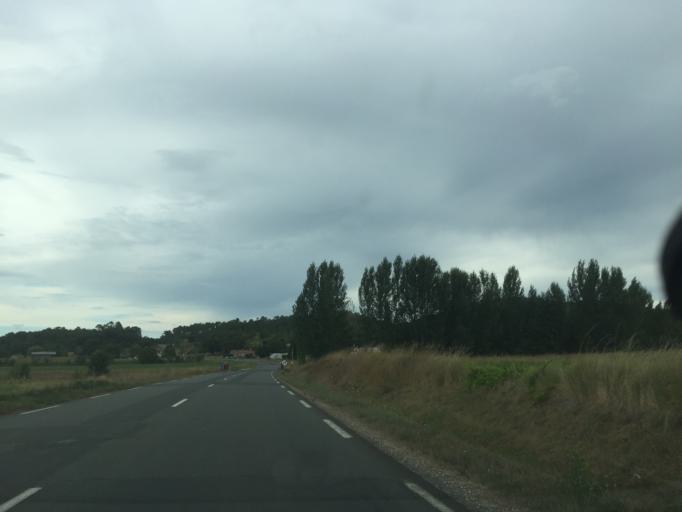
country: FR
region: Aquitaine
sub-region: Departement du Lot-et-Garonne
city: Fumel
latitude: 44.5171
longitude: 0.9475
